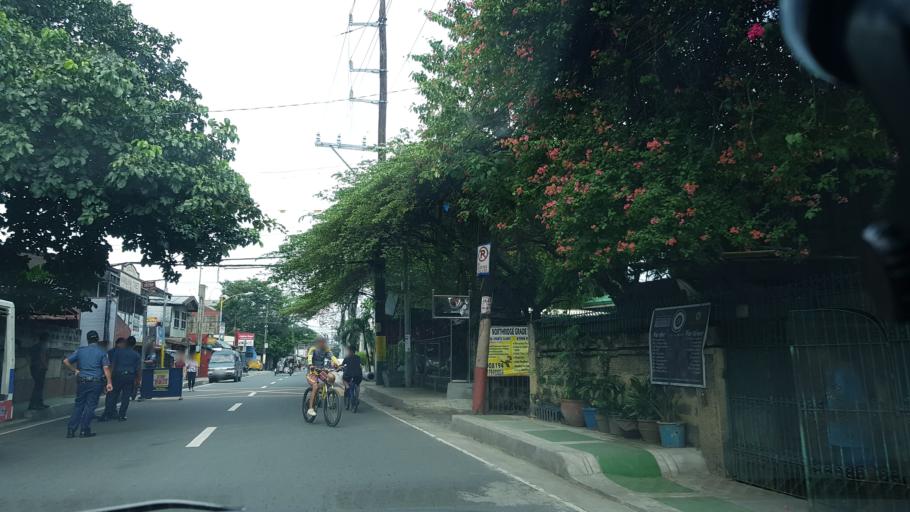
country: PH
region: Metro Manila
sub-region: Pasig
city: Pasig City
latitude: 14.5750
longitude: 121.0793
